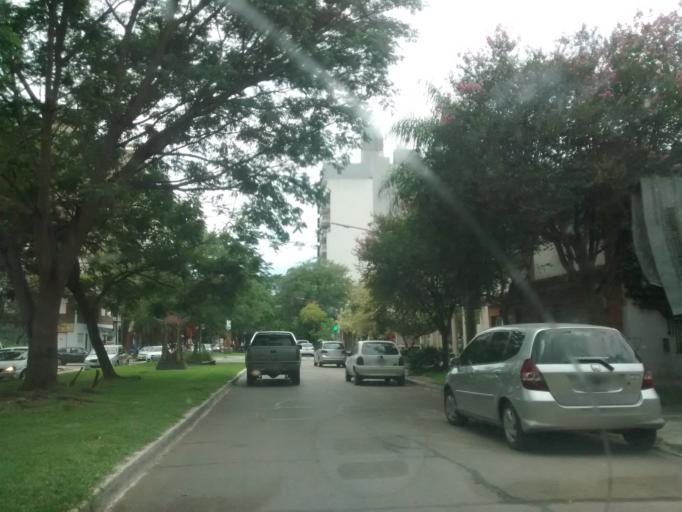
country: AR
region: Chaco
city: Resistencia
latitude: -27.4461
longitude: -58.9808
